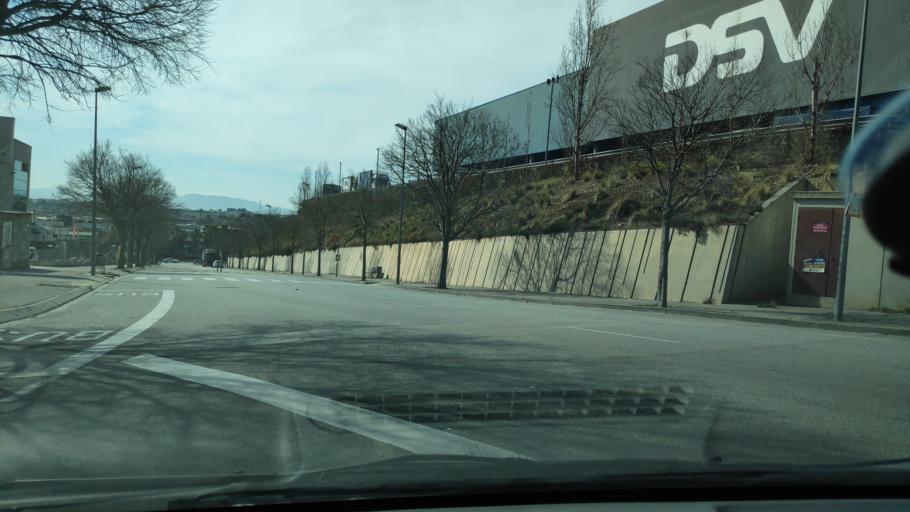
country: ES
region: Catalonia
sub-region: Provincia de Barcelona
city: Rubi
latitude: 41.5082
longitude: 2.0385
